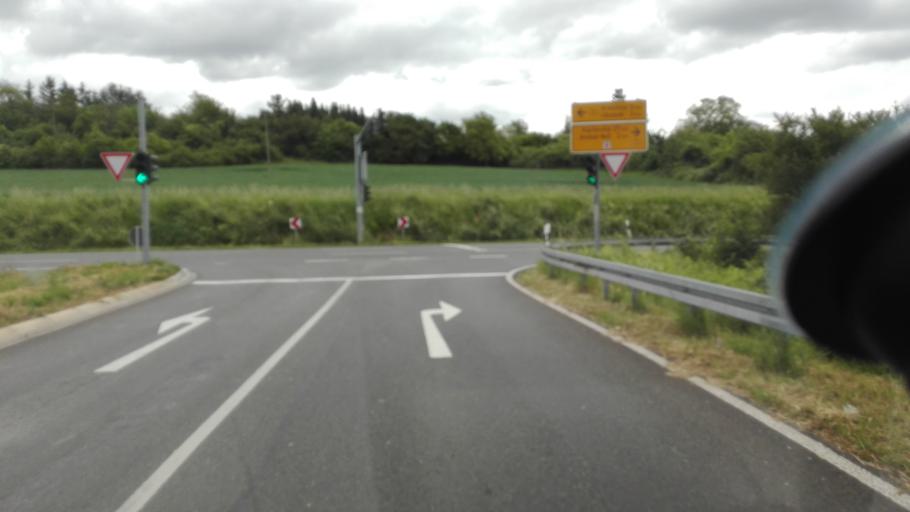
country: DE
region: Baden-Wuerttemberg
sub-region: Karlsruhe Region
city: Bruchsal
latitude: 49.1426
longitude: 8.6082
